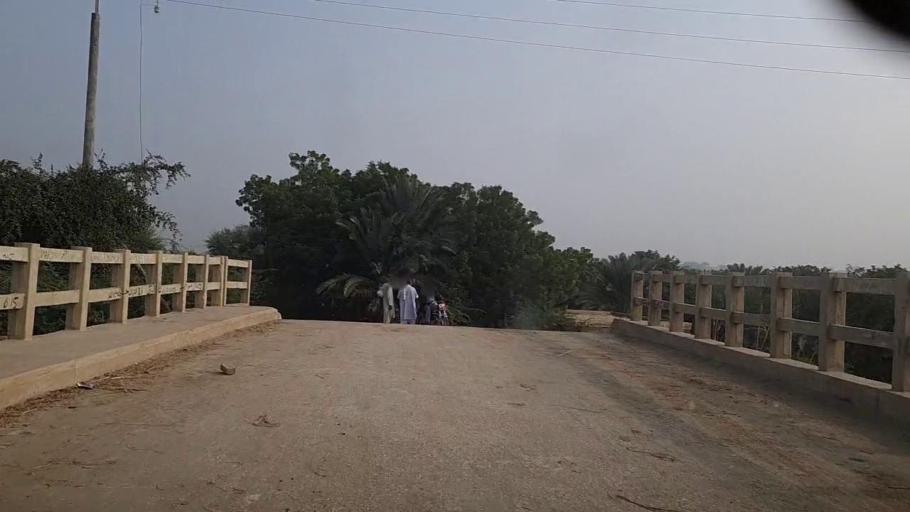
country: PK
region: Sindh
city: Bozdar
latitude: 27.1346
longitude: 68.6533
